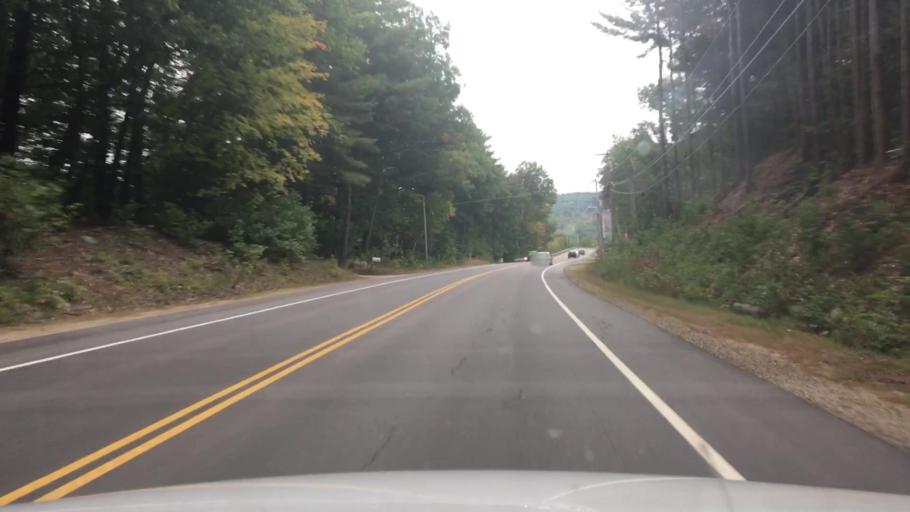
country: US
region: New Hampshire
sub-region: Strafford County
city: New Durham
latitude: 43.4862
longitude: -71.2479
